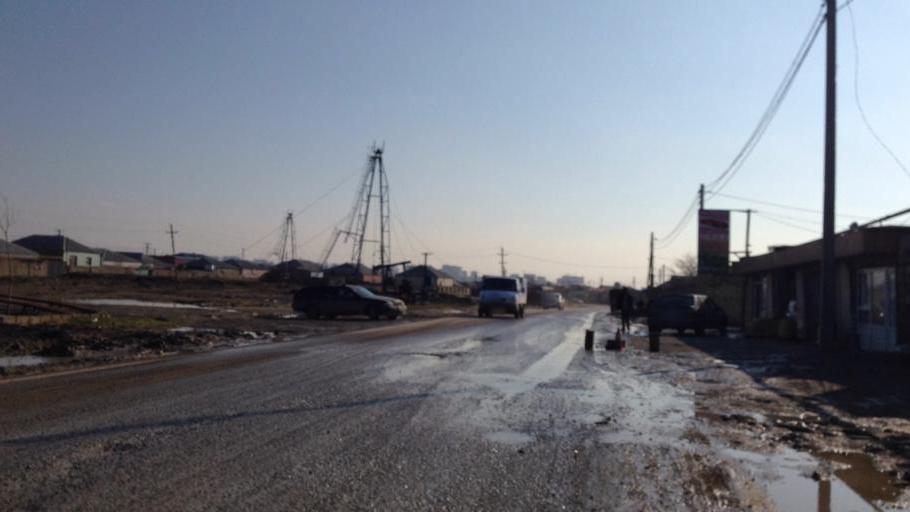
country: AZ
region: Baki
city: Balakhani
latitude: 40.4504
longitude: 49.9315
